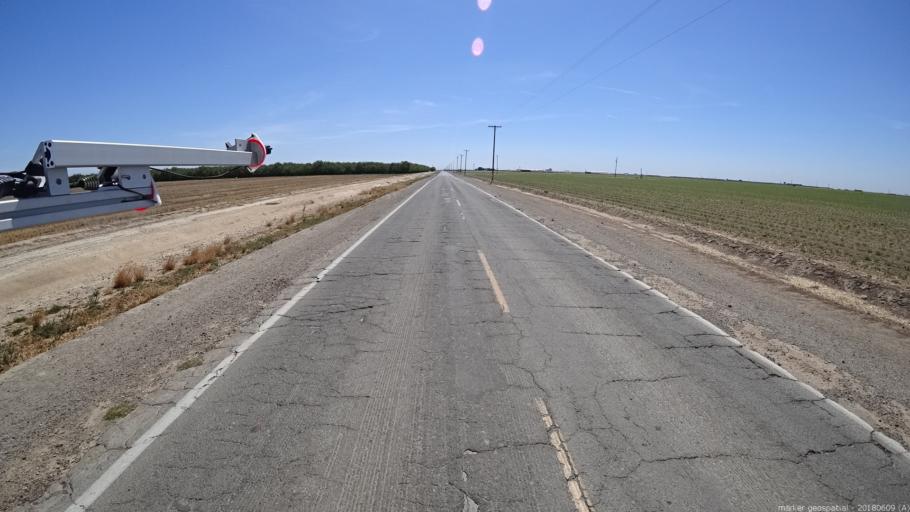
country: US
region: California
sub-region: Madera County
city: Fairmead
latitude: 36.9528
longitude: -120.2629
